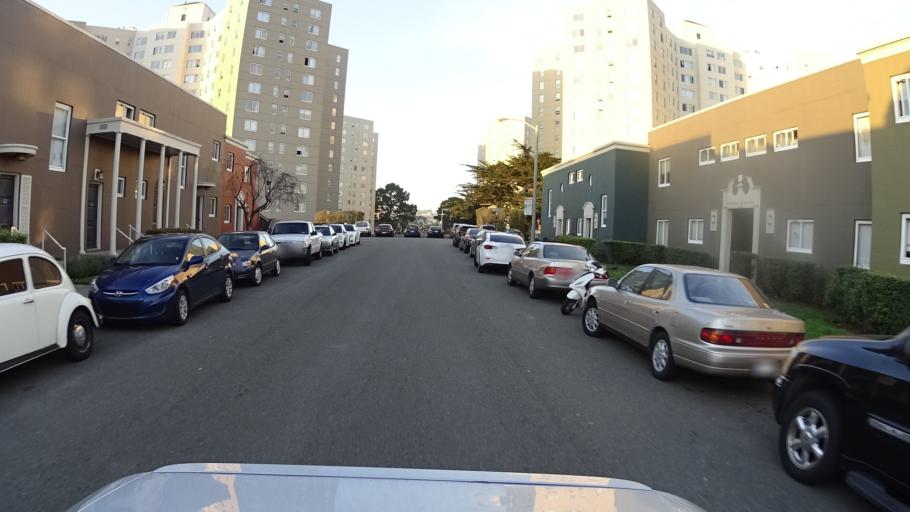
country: US
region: California
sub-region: San Mateo County
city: Daly City
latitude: 37.7170
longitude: -122.4816
